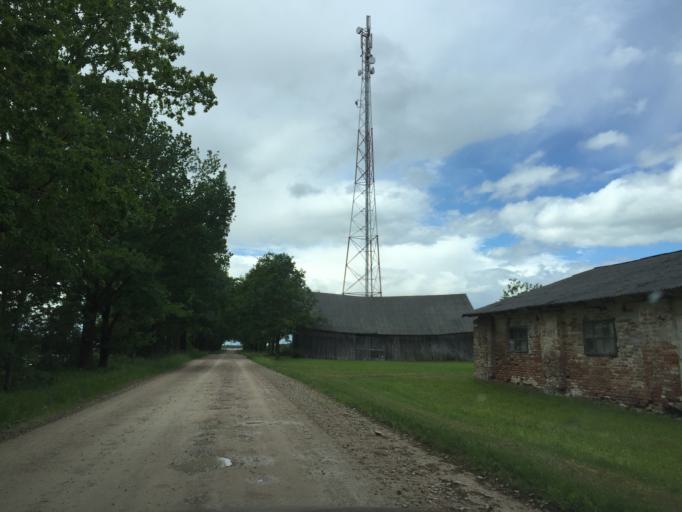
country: LV
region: Lecava
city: Iecava
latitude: 56.5830
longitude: 24.1887
